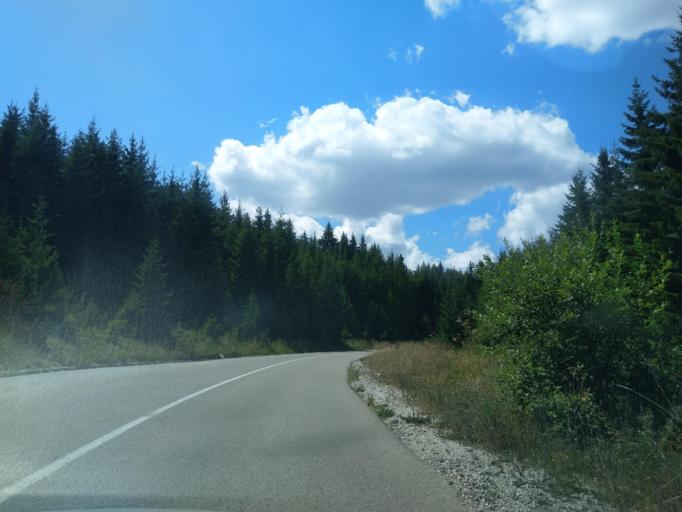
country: RS
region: Central Serbia
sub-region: Zlatiborski Okrug
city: Nova Varos
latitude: 43.3271
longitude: 19.8612
